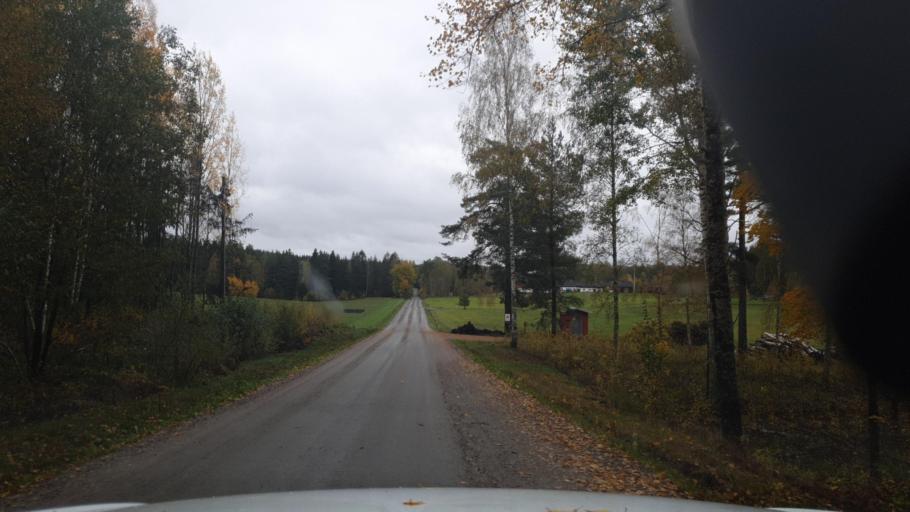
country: SE
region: Vaermland
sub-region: Karlstads Kommun
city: Edsvalla
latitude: 59.4869
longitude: 13.0376
